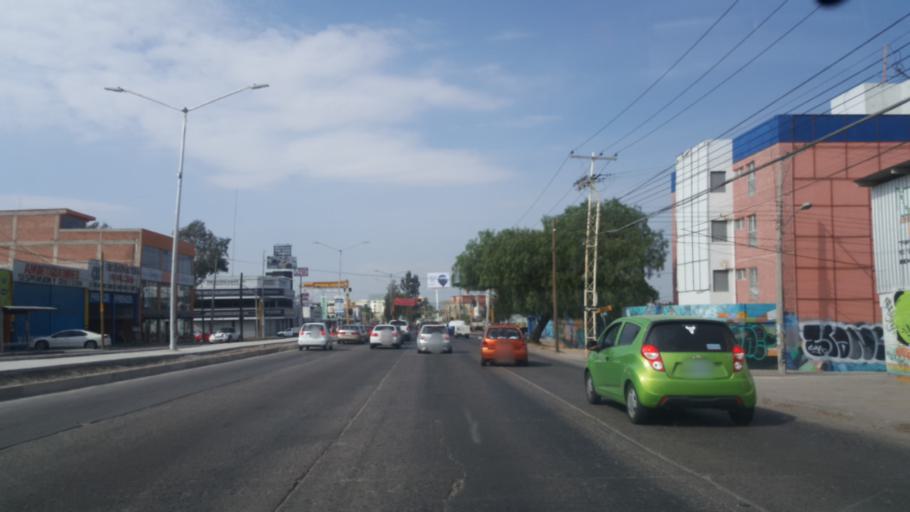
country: MX
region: Guanajuato
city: Leon
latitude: 21.0976
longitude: -101.6401
